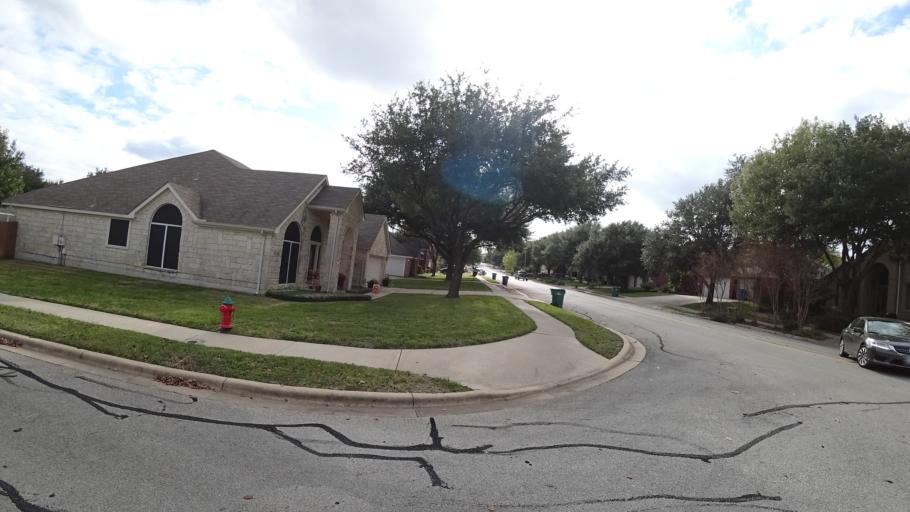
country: US
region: Texas
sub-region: Travis County
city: Pflugerville
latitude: 30.4333
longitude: -97.6270
